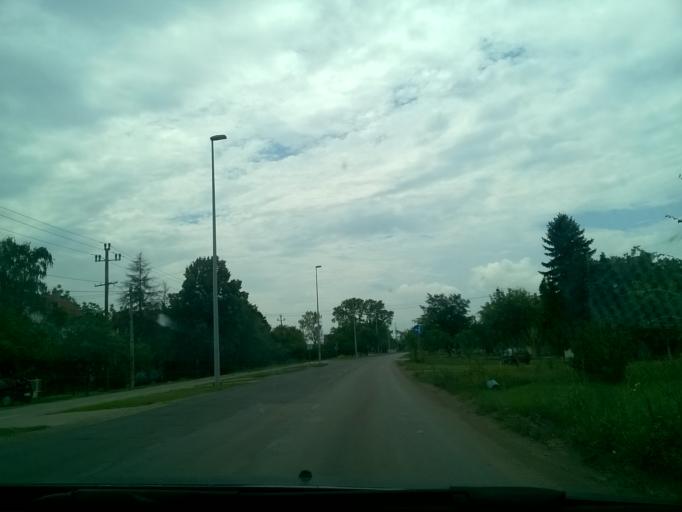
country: RS
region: Autonomna Pokrajina Vojvodina
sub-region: Srednjebanatski Okrug
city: Zrenjanin
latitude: 45.3997
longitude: 20.3931
